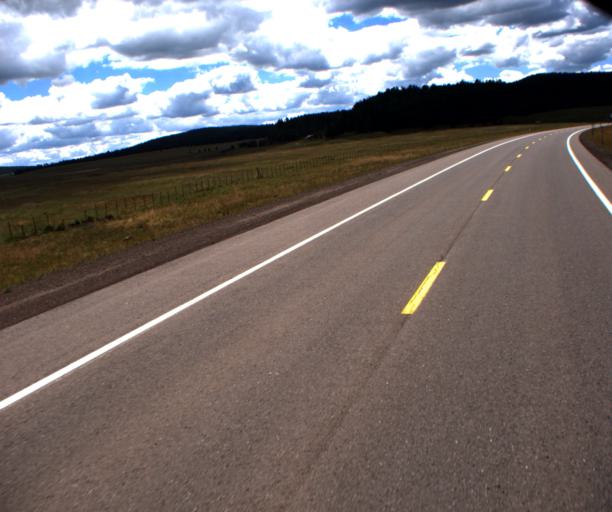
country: US
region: Arizona
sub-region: Apache County
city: Eagar
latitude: 34.0144
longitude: -109.5677
